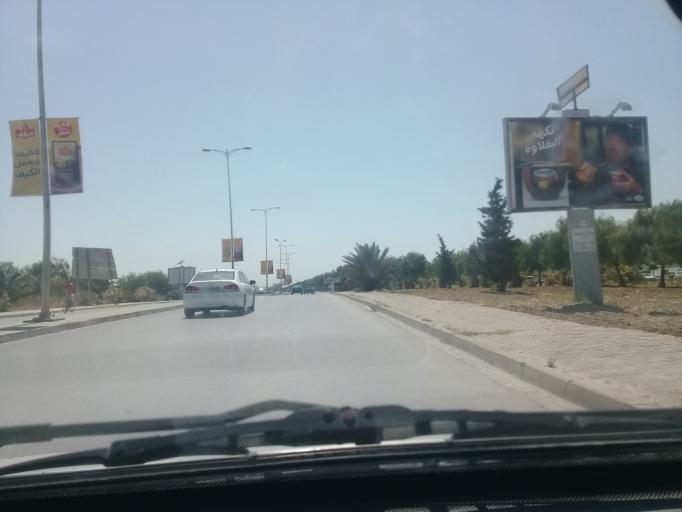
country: TN
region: Tunis
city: La Goulette
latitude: 36.8456
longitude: 10.2573
